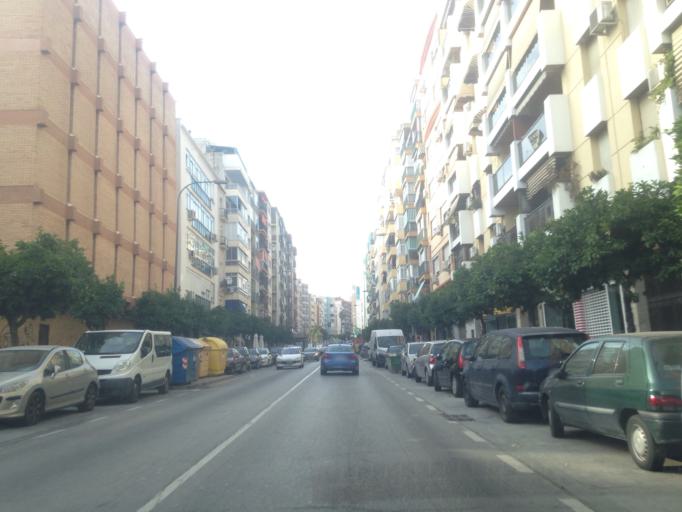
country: ES
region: Andalusia
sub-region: Provincia de Malaga
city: Malaga
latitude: 36.7316
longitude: -4.4153
